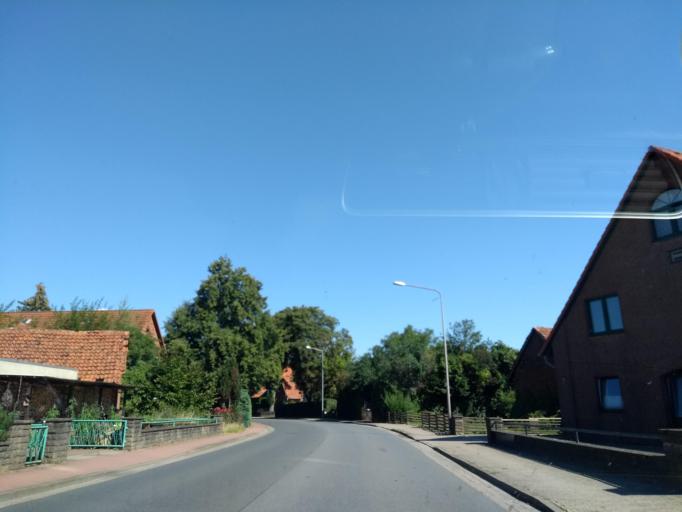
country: DE
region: Lower Saxony
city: Wunstorf
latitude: 52.4504
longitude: 9.4195
